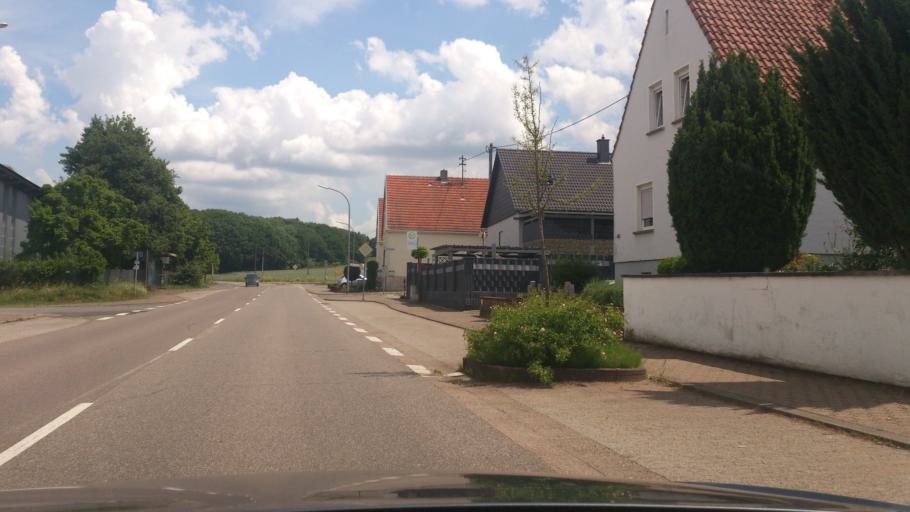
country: DE
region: Saarland
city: Schwalbach
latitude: 49.3092
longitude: 6.8328
